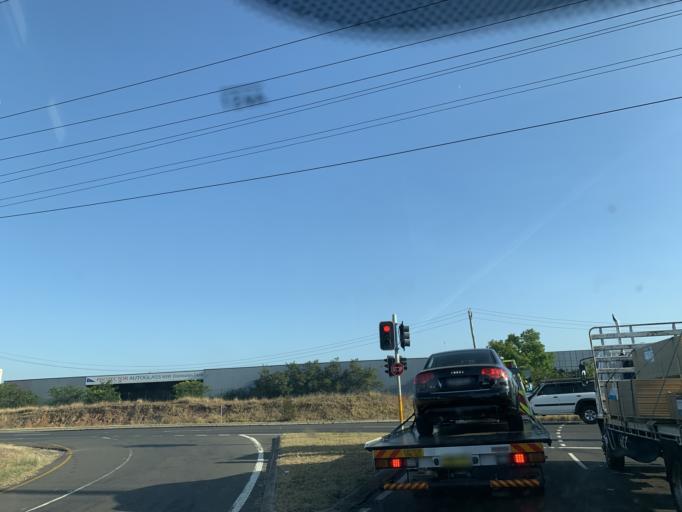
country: AU
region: New South Wales
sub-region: Blacktown
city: Doonside
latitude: -33.7958
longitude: 150.8886
